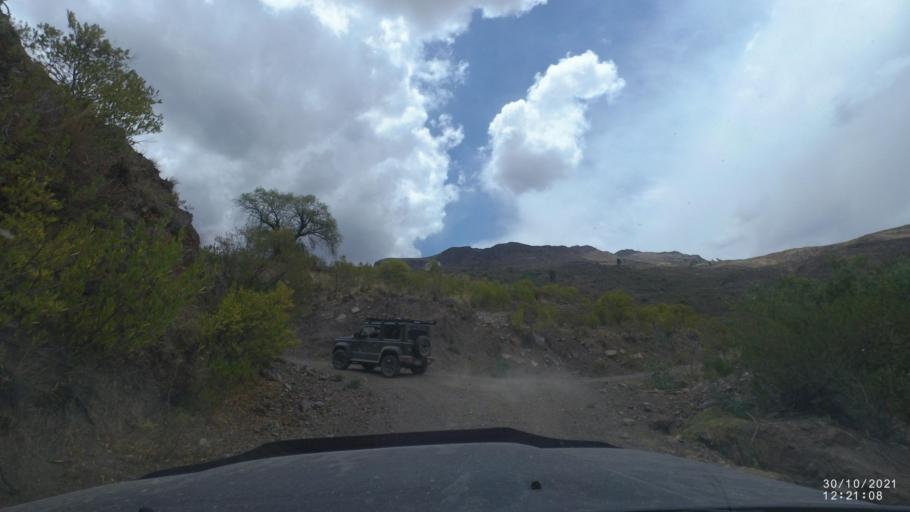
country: BO
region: Cochabamba
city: Colchani
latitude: -17.5709
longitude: -66.6317
